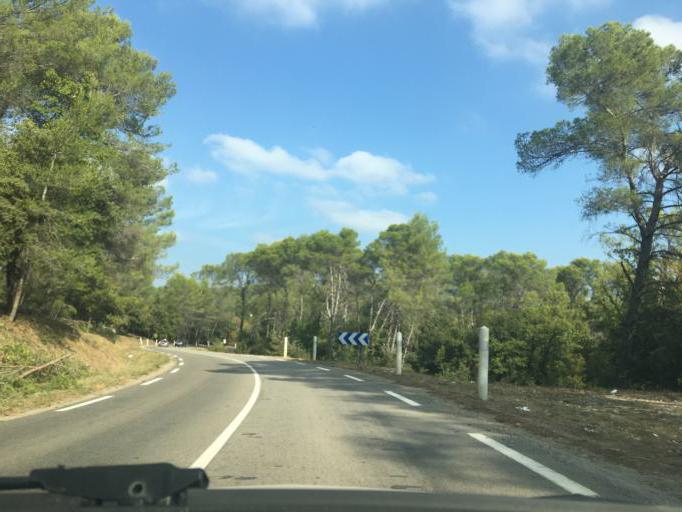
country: FR
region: Provence-Alpes-Cote d'Azur
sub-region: Departement du Var
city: Flayosc
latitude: 43.5045
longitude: 6.4213
